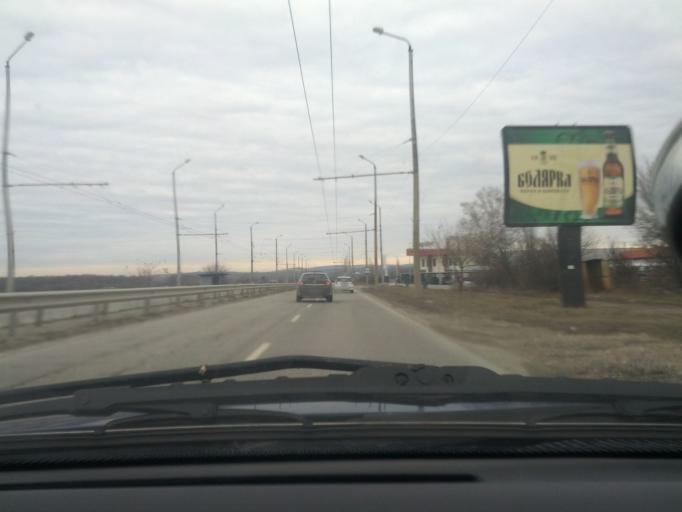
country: BG
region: Vratsa
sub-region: Obshtina Vratsa
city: Vratsa
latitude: 43.2286
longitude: 23.5620
